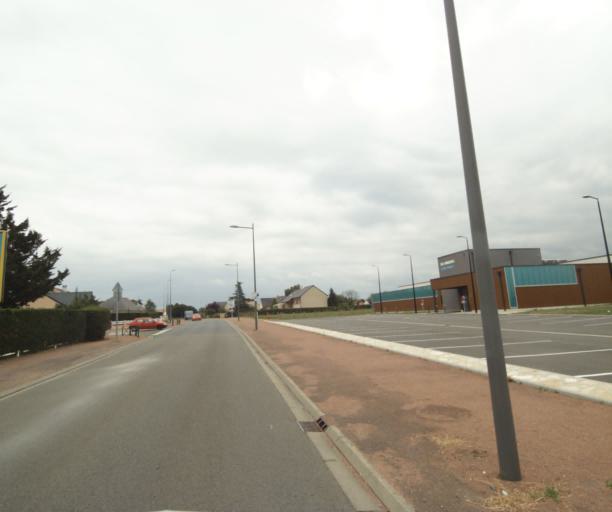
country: FR
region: Pays de la Loire
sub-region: Departement de la Sarthe
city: Sable-sur-Sarthe
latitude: 47.8286
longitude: -0.3196
